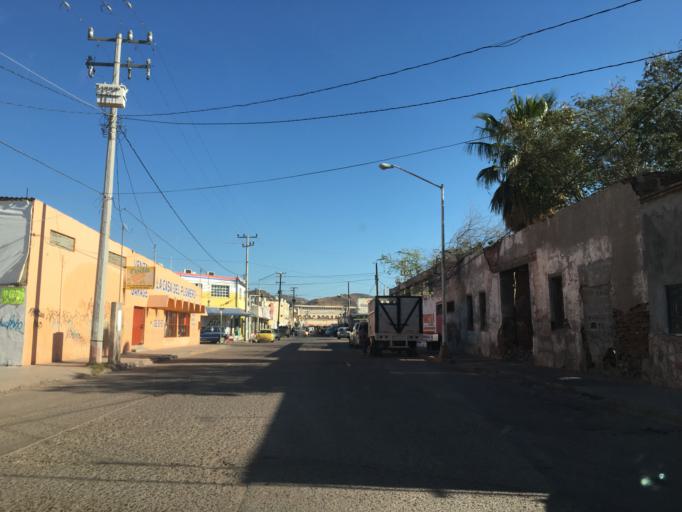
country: MX
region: Sonora
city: Heroica Guaymas
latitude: 27.9206
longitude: -110.8935
